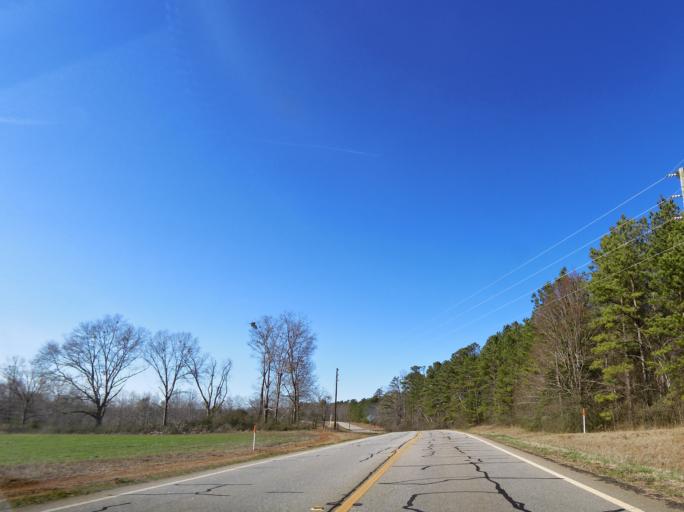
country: US
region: Georgia
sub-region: Lamar County
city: Barnesville
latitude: 32.9034
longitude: -84.1146
